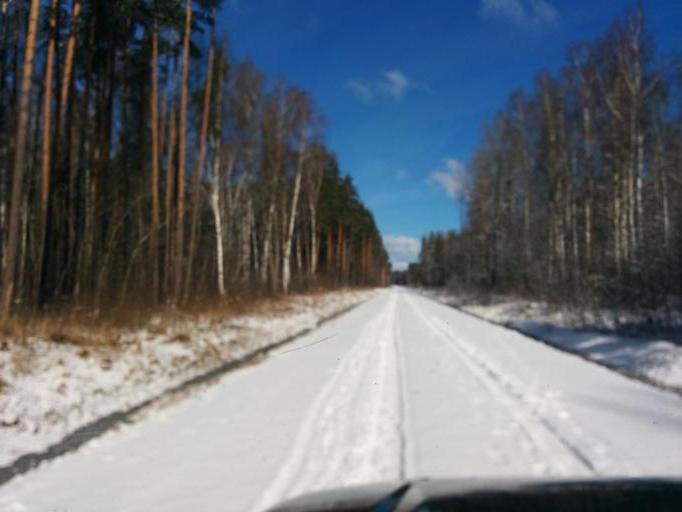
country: LV
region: Jelgava
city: Jelgava
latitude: 56.6161
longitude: 23.6689
